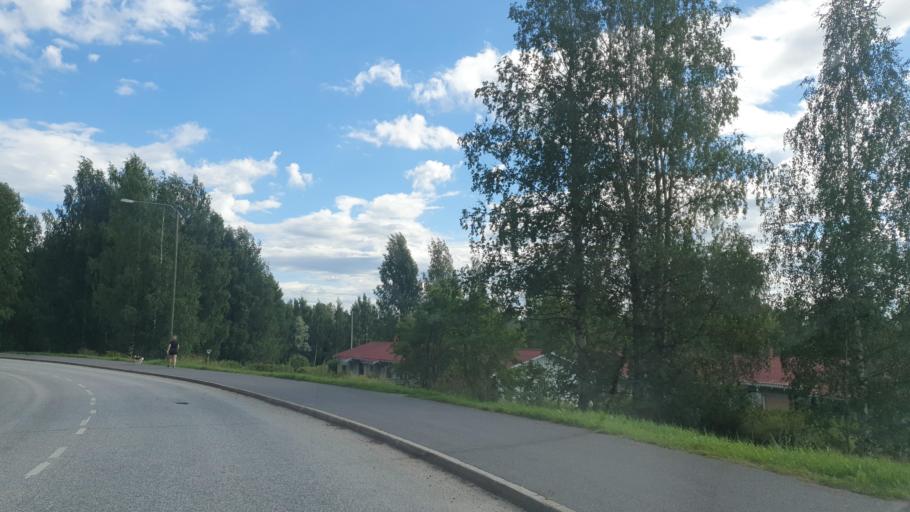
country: FI
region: Central Finland
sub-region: Jyvaeskylae
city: Saeynaetsalo
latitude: 62.1553
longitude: 25.7571
